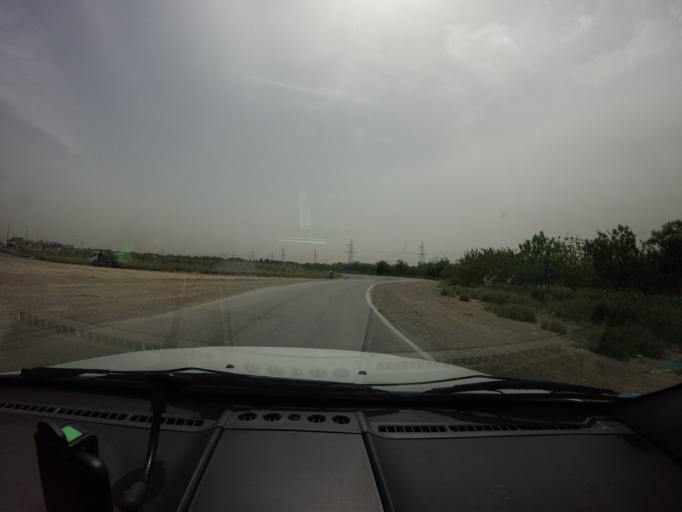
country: IR
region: Tehran
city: Eslamshahr
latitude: 35.6215
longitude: 51.2285
